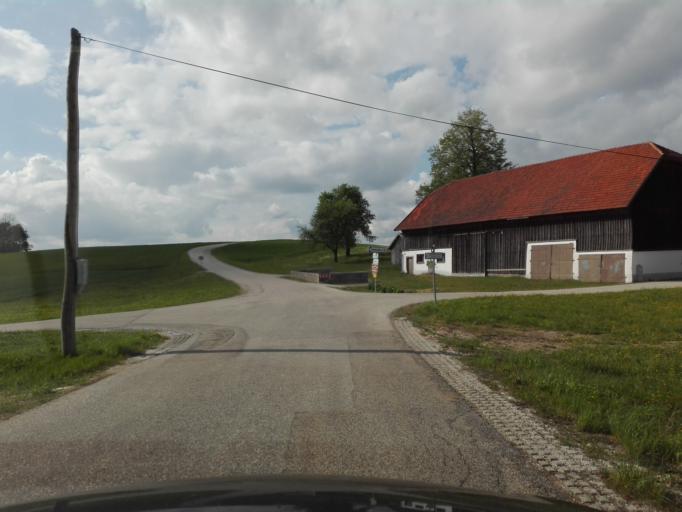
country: AT
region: Upper Austria
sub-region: Politischer Bezirk Rohrbach
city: Pfarrkirchen im Muehlkreis
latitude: 48.4231
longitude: 13.8432
